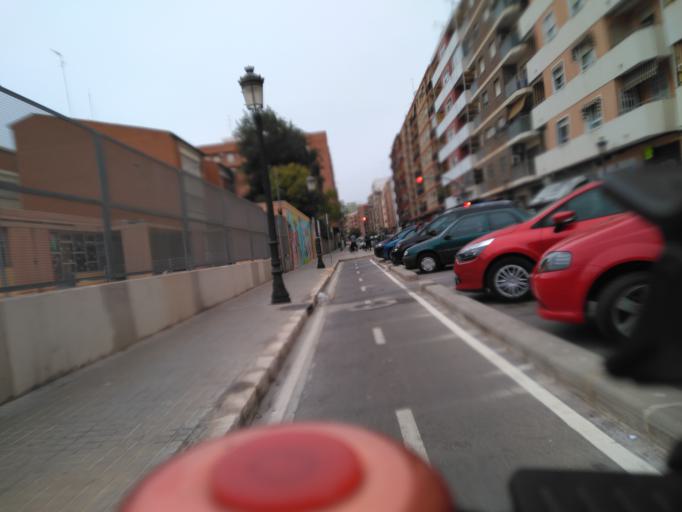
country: ES
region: Valencia
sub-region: Provincia de Valencia
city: Valencia
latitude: 39.4702
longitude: -0.3954
